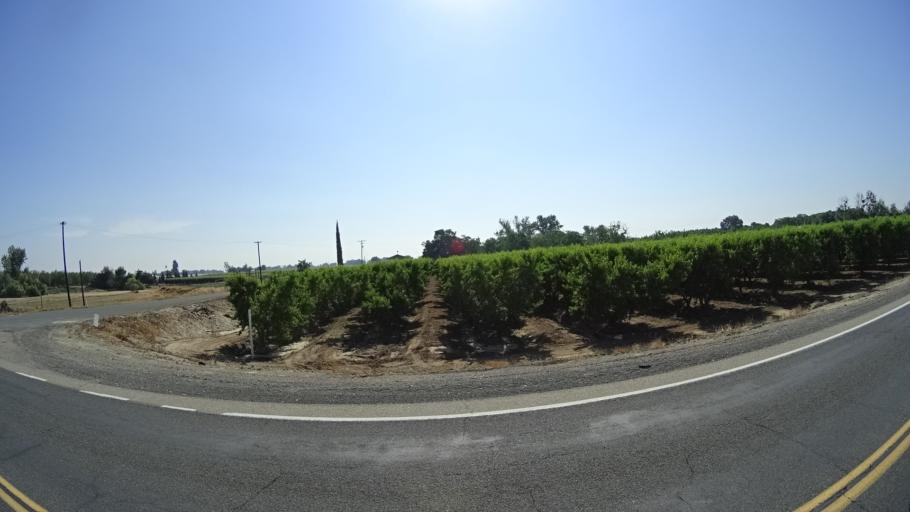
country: US
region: California
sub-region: Fresno County
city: Kingsburg
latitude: 36.4486
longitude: -119.5647
